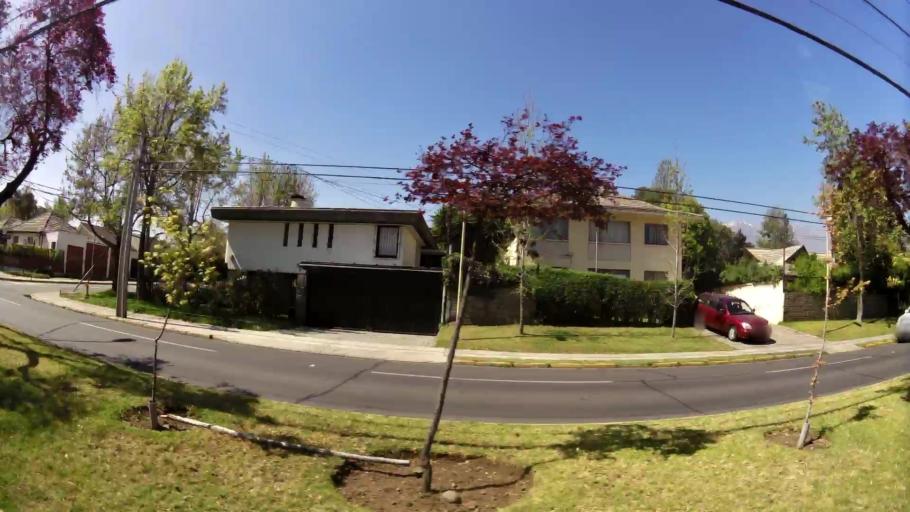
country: CL
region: Santiago Metropolitan
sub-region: Provincia de Santiago
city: Villa Presidente Frei, Nunoa, Santiago, Chile
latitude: -33.4235
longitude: -70.5706
